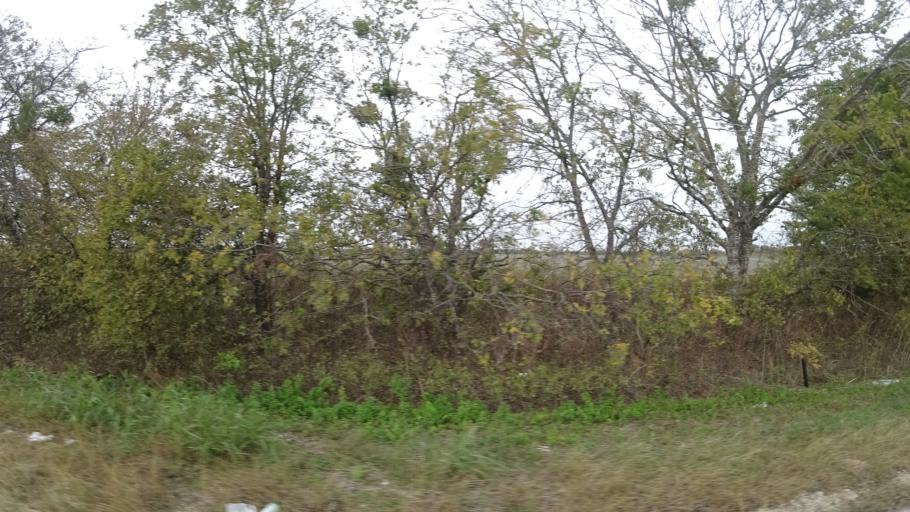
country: US
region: Texas
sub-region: Travis County
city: Pflugerville
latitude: 30.3924
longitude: -97.5966
